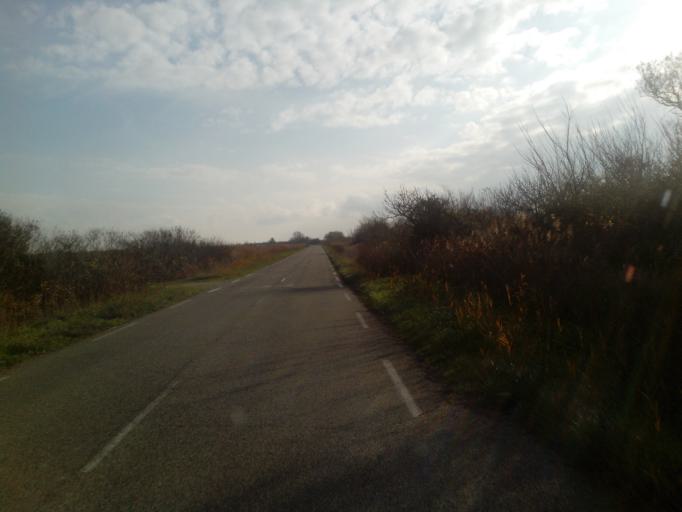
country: FR
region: Languedoc-Roussillon
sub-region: Departement du Gard
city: Saint-Gilles
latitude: 43.5978
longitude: 4.4898
